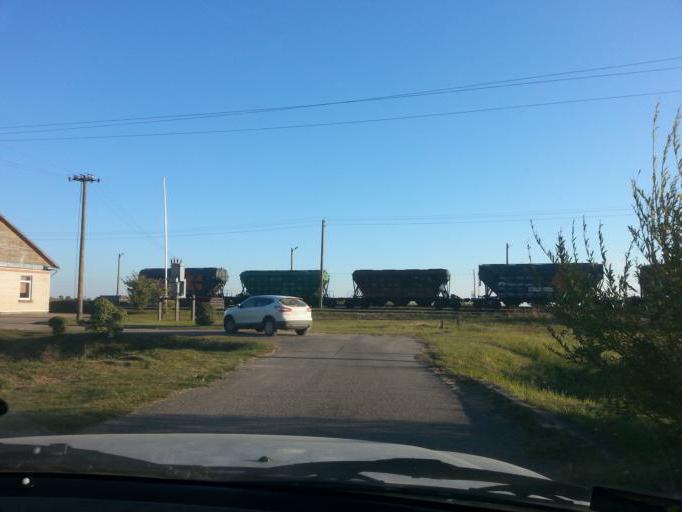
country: LV
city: Tervete
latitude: 56.6001
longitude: 23.4938
